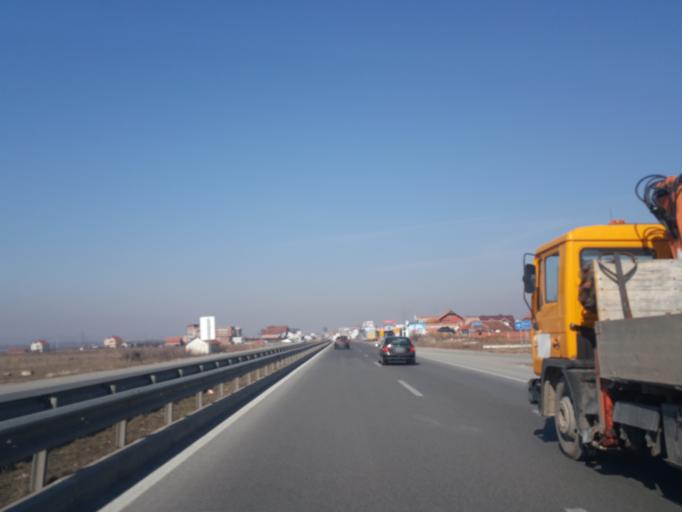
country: XK
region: Pristina
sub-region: Komuna e Obiliqit
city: Obiliq
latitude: 42.7610
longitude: 21.0303
